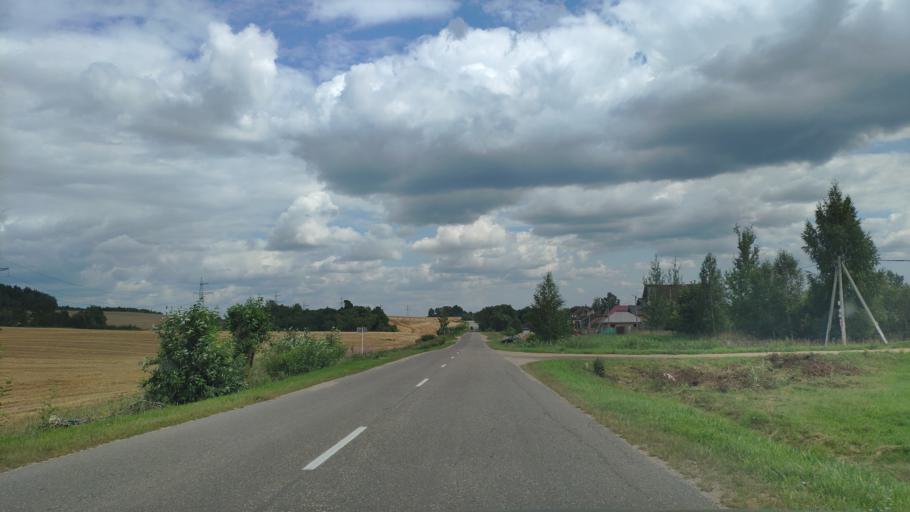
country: BY
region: Minsk
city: Khatsyezhyna
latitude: 53.8722
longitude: 27.3055
